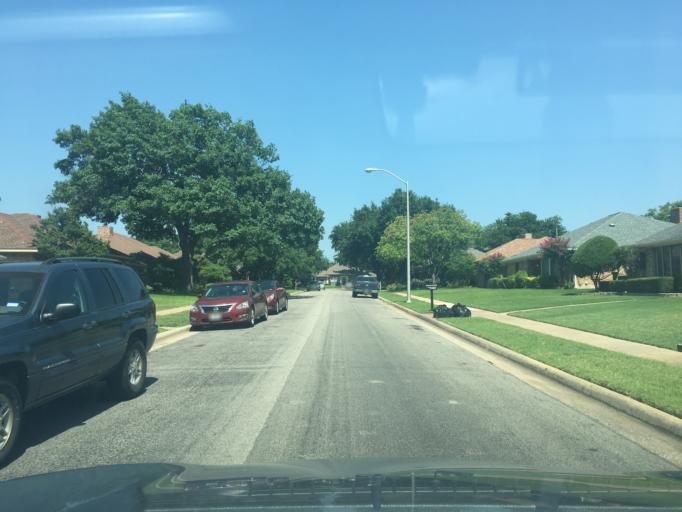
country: US
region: Texas
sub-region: Dallas County
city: Richardson
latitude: 32.9267
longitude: -96.7077
